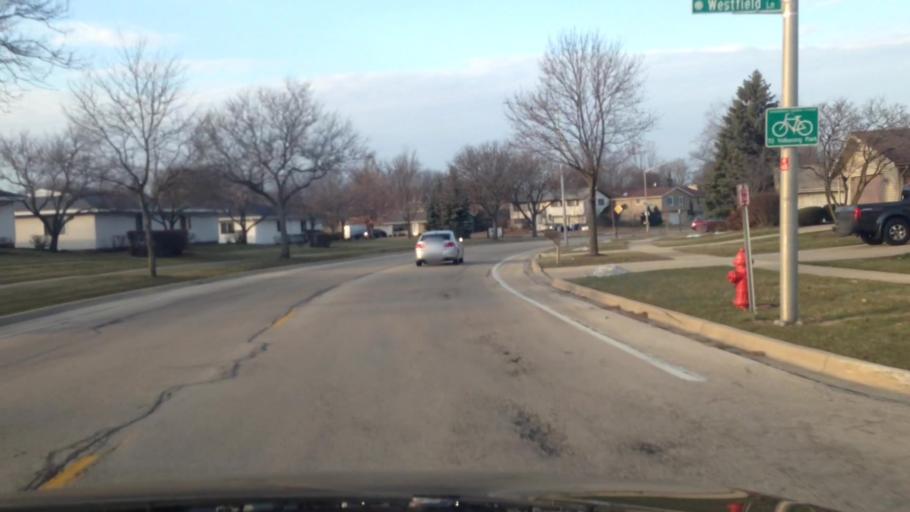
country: US
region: Illinois
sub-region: Cook County
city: Schaumburg
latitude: 42.0087
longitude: -88.1020
